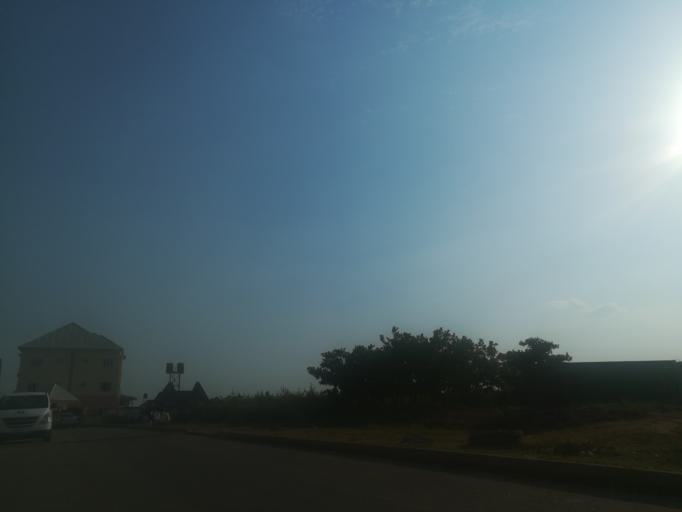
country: NG
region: Abuja Federal Capital Territory
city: Abuja
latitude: 9.0466
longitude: 7.4384
